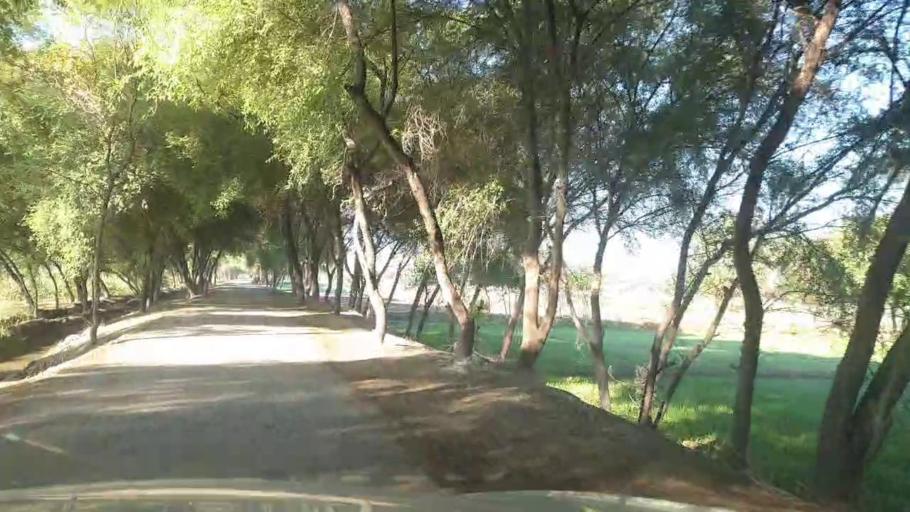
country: PK
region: Sindh
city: Bhan
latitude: 26.5509
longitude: 67.6804
